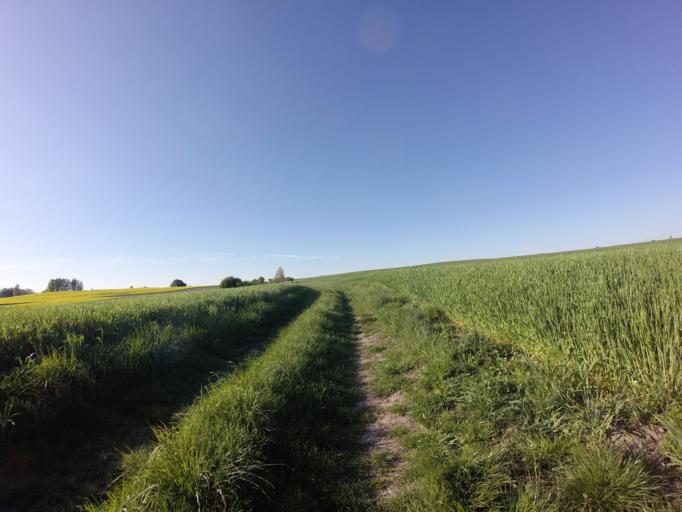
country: PL
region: West Pomeranian Voivodeship
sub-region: Powiat choszczenski
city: Choszczno
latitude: 53.1258
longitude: 15.3596
